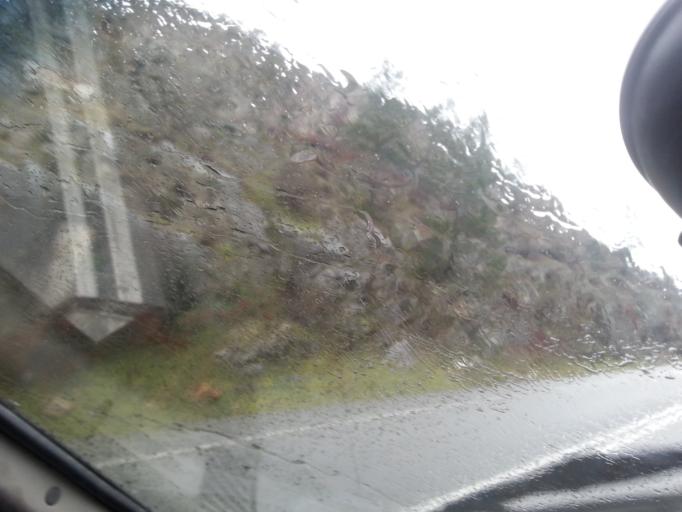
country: PT
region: Guarda
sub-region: Fornos de Algodres
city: Fornos de Algodres
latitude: 40.6044
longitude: -7.5844
